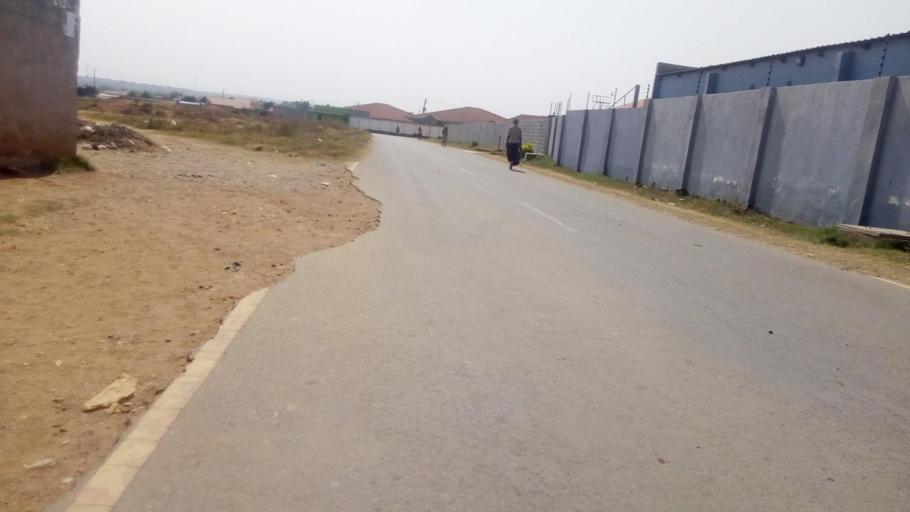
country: ZM
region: Lusaka
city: Lusaka
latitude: -15.3601
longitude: 28.2833
